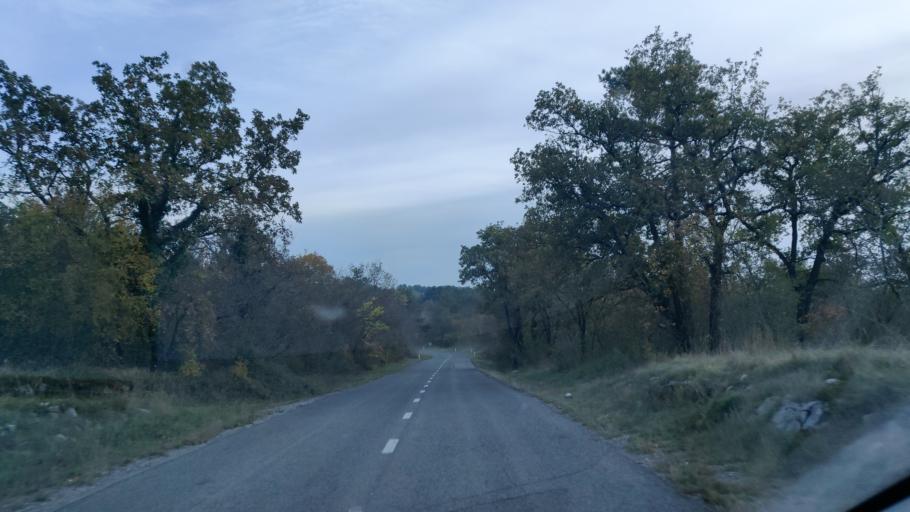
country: SI
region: Sezana
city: Sezana
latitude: 45.7965
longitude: 13.8555
